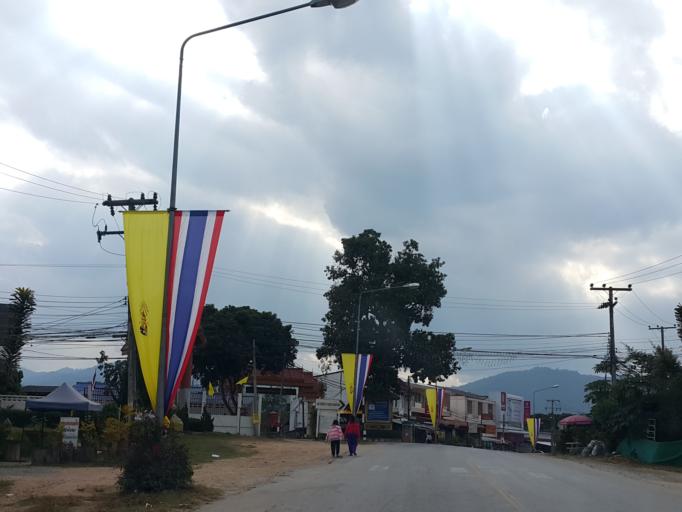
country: TH
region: Chiang Mai
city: Om Koi
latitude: 17.8013
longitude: 98.3610
